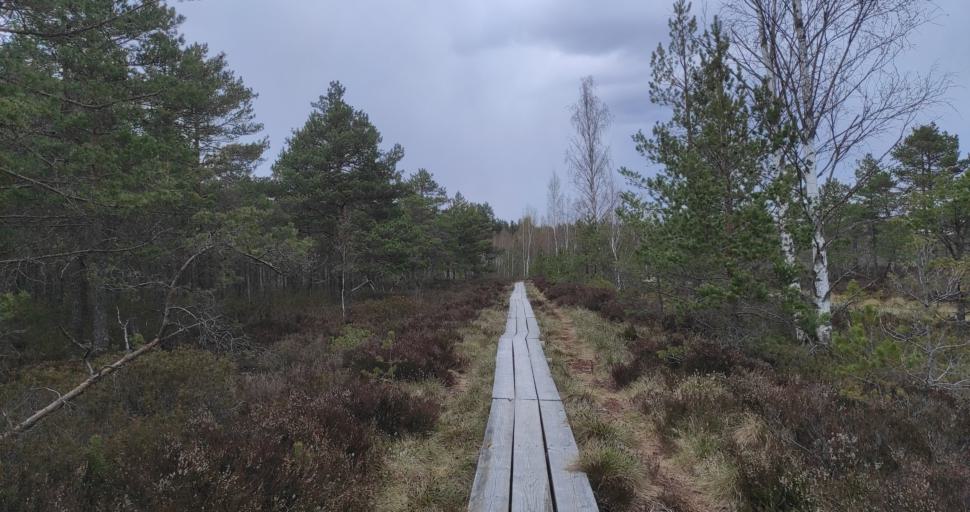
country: LV
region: Dundaga
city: Dundaga
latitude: 57.3520
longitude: 22.1501
